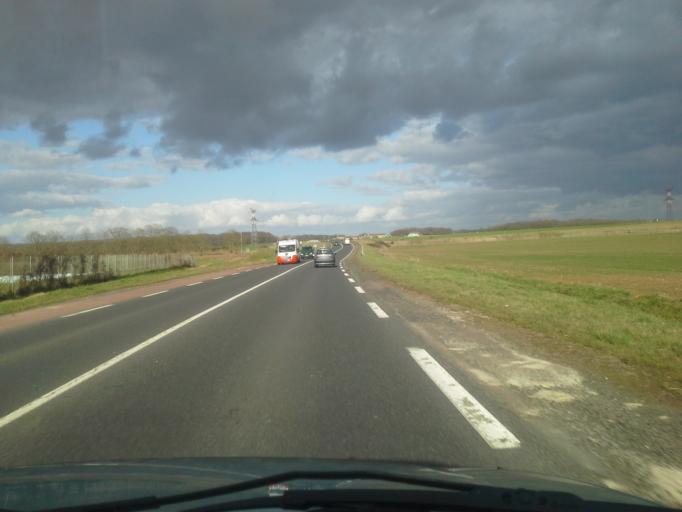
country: FR
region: Centre
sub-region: Departement d'Indre-et-Loire
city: Parcay-Meslay
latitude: 47.4714
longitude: 0.7535
